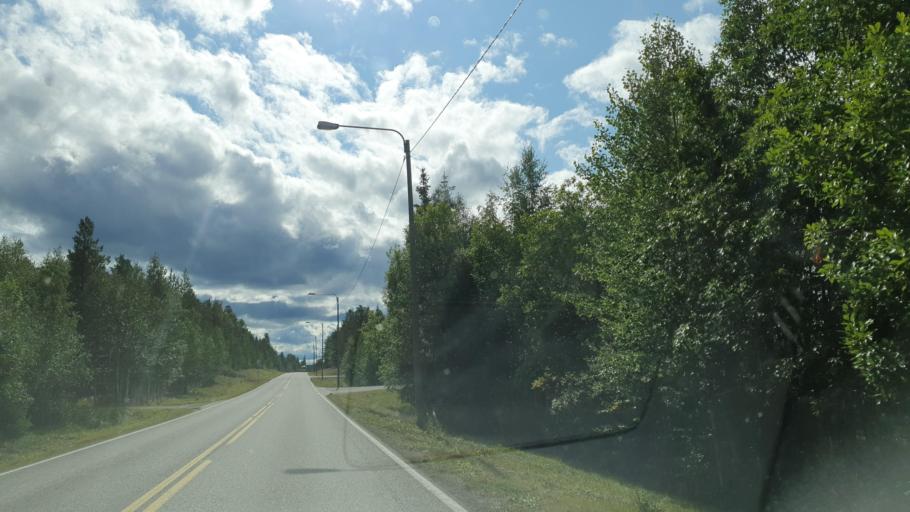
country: FI
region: Lapland
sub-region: Tunturi-Lappi
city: Muonio
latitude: 67.8890
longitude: 24.2152
